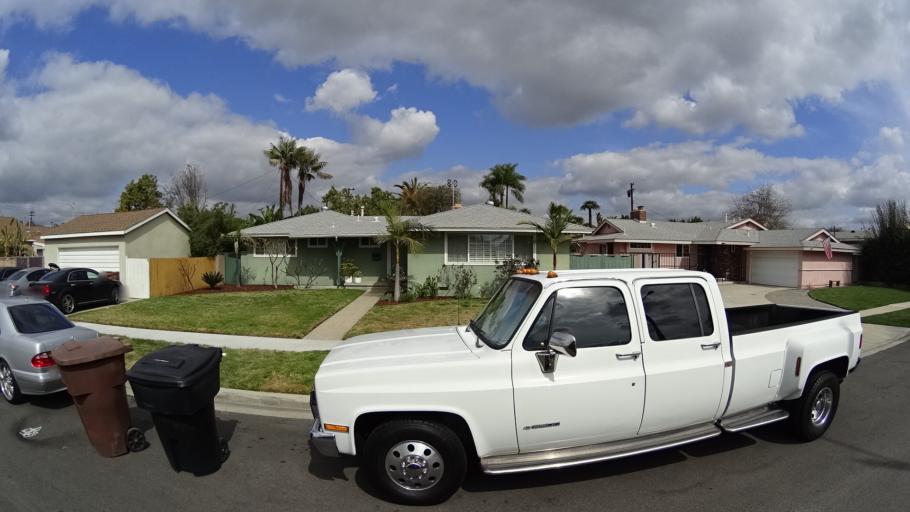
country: US
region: California
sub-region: Orange County
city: Stanton
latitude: 33.8349
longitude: -117.9785
